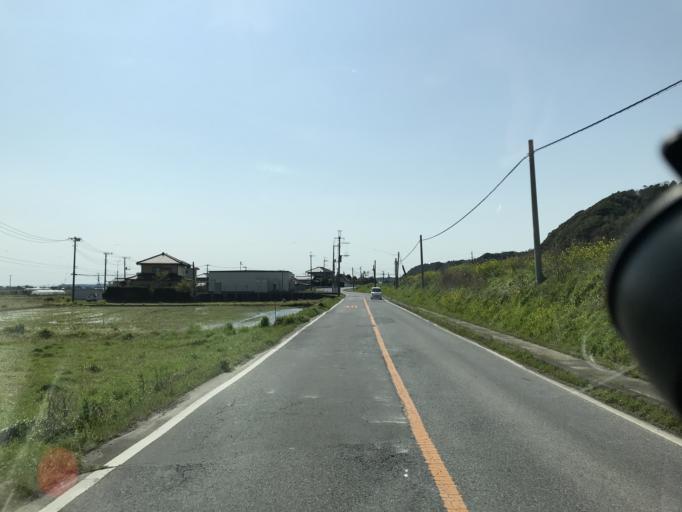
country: JP
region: Chiba
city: Asahi
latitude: 35.7641
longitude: 140.6137
